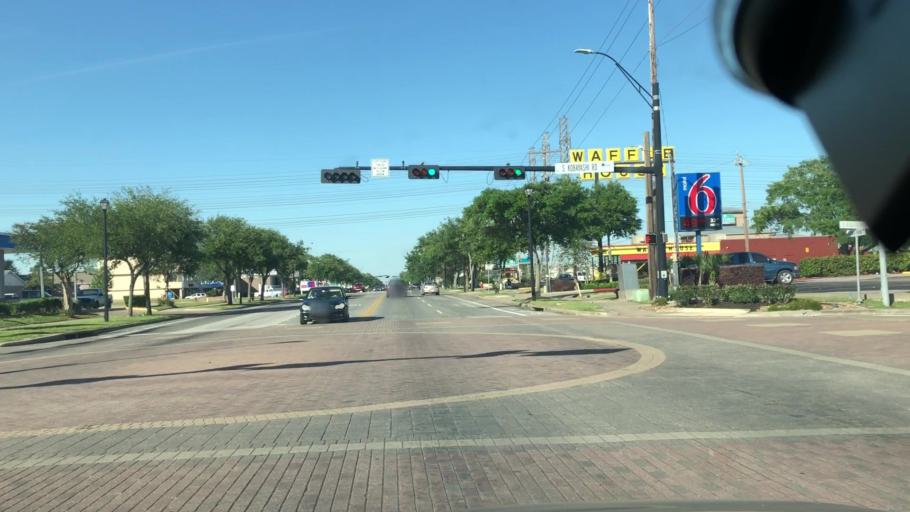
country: US
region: Texas
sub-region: Harris County
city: Webster
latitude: 29.5308
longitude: -95.1275
